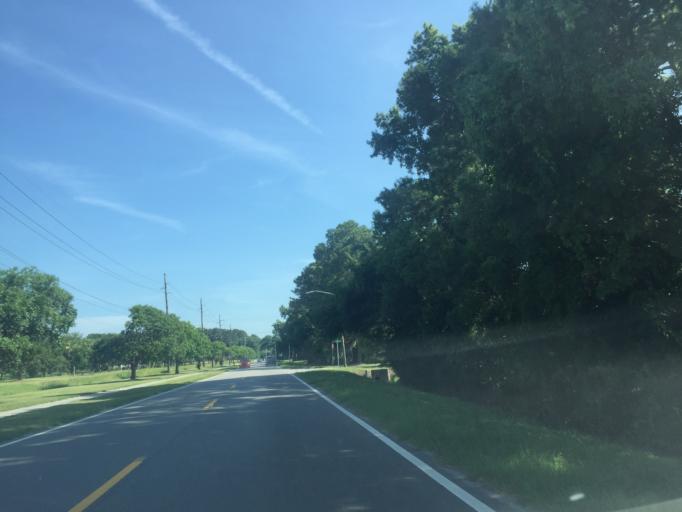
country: US
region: Georgia
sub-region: Chatham County
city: Isle of Hope
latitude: 31.9954
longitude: -81.0905
